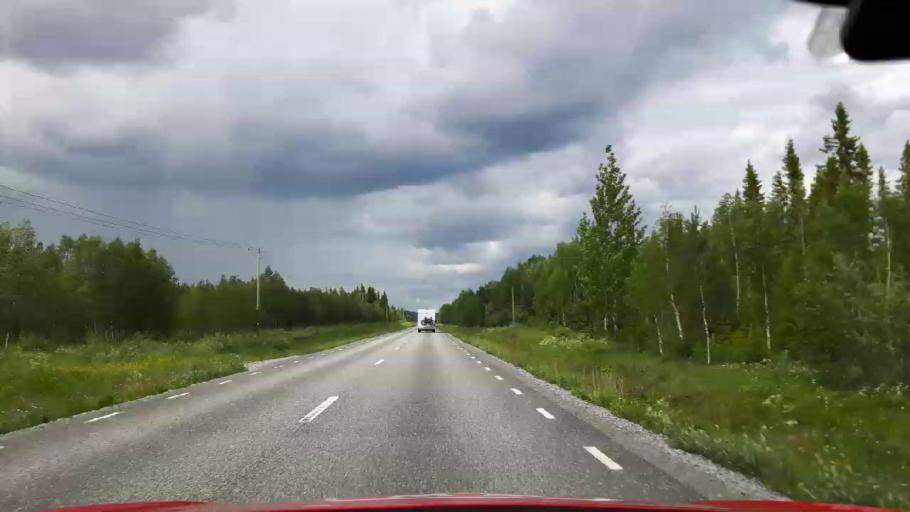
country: SE
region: Jaemtland
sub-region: Krokoms Kommun
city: Krokom
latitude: 63.6593
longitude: 14.3642
